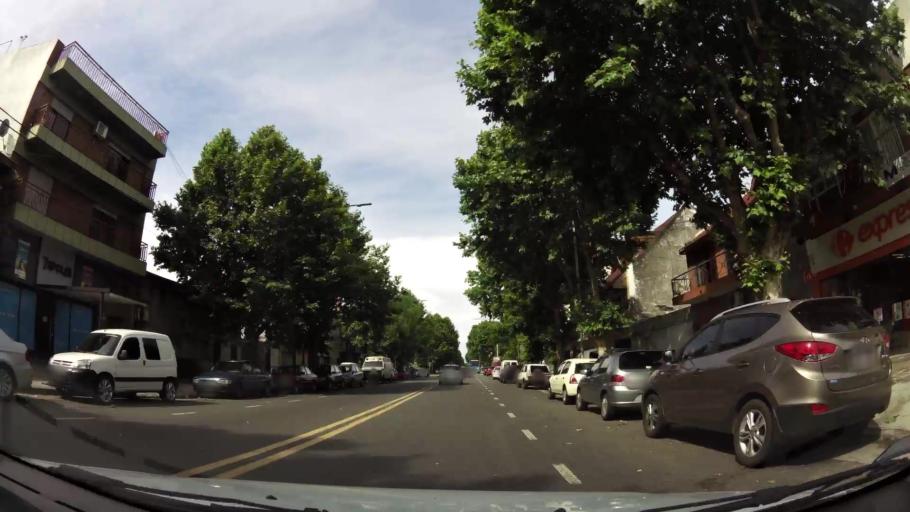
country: AR
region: Buenos Aires F.D.
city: Villa Santa Rita
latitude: -34.6488
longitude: -58.5086
